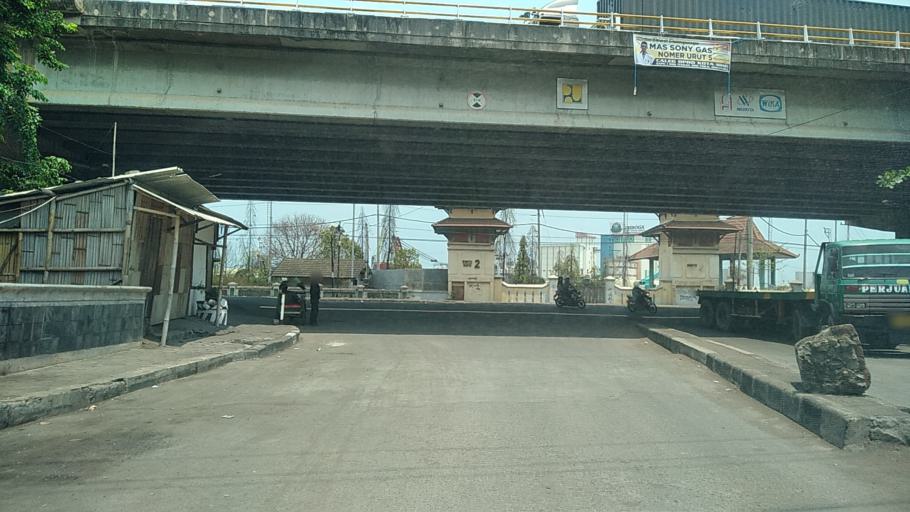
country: ID
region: Central Java
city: Semarang
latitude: -6.9570
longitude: 110.4243
